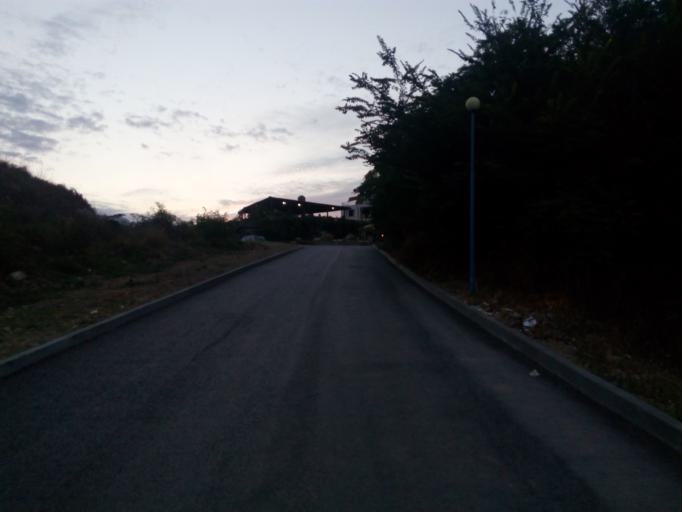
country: BG
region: Burgas
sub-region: Obshtina Nesebur
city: Obzor
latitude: 42.8158
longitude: 27.8853
